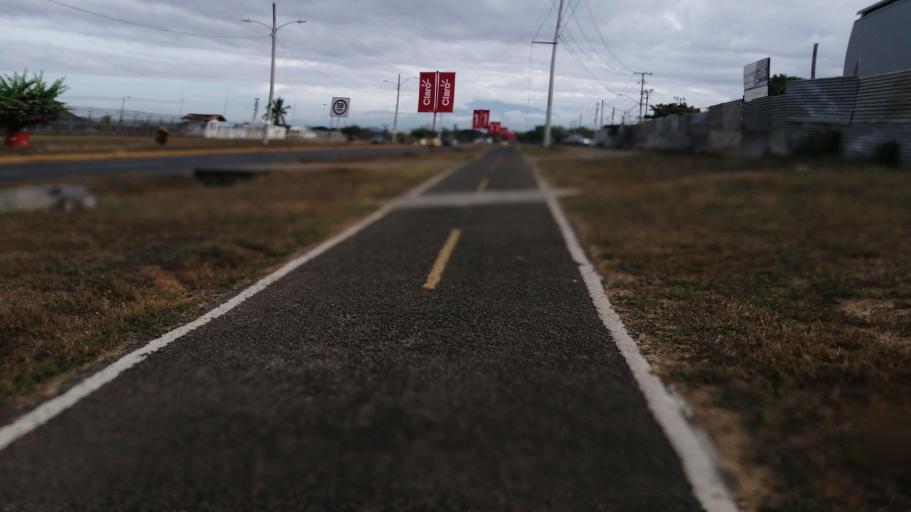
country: PA
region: Chiriqui
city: Pedregal
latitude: 8.3953
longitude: -82.4276
